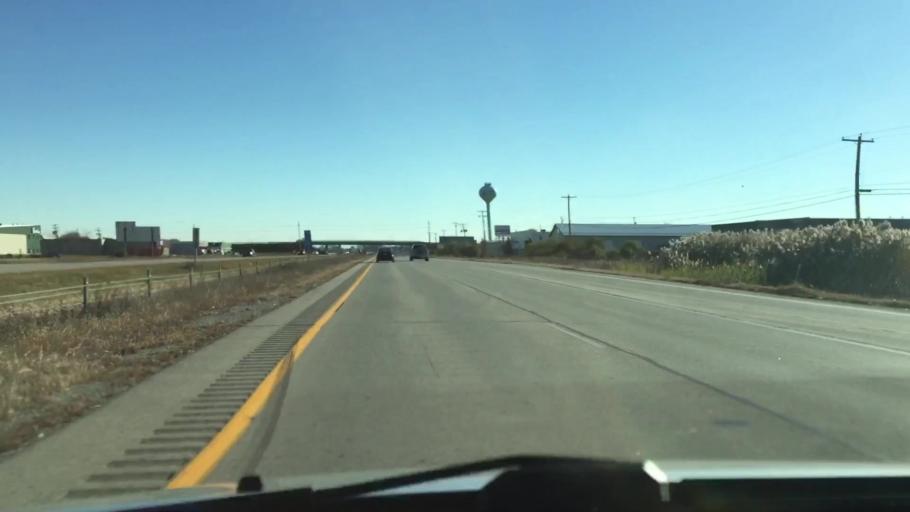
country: US
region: Wisconsin
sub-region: Outagamie County
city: Little Chute
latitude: 44.2977
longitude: -88.3092
